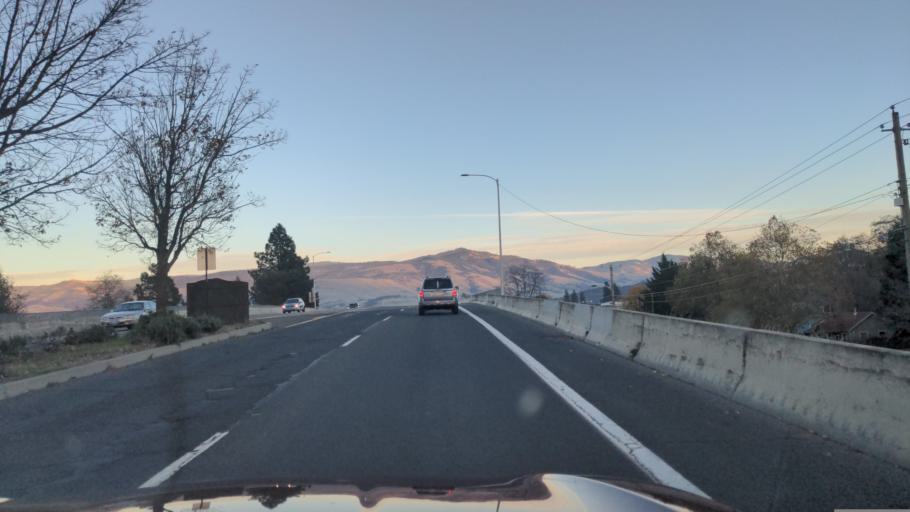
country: US
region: Oregon
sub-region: Jackson County
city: Ashland
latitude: 42.1853
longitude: -122.6782
